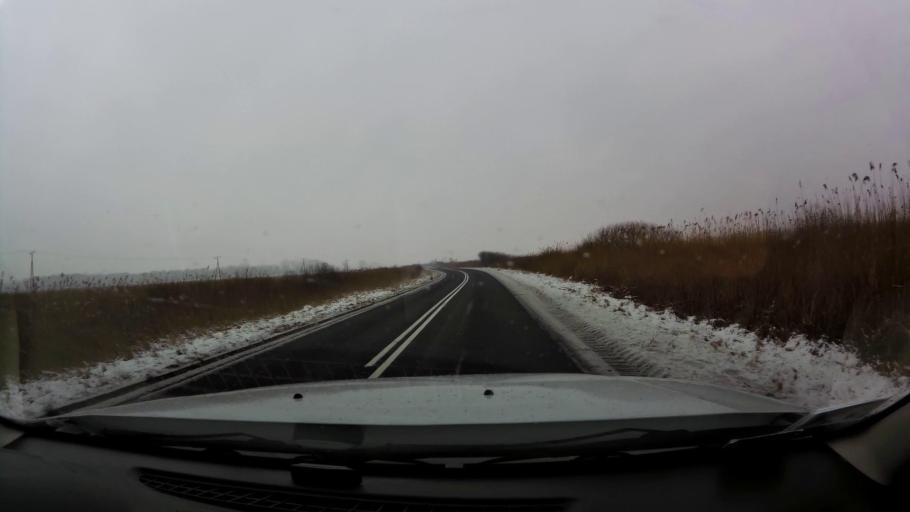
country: PL
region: West Pomeranian Voivodeship
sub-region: Powiat gryficki
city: Mrzezyno
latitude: 54.1152
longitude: 15.2664
